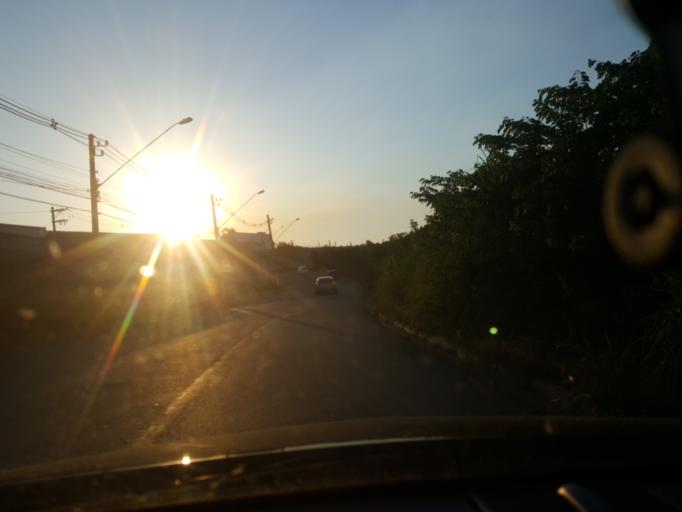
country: BR
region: Sao Paulo
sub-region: Cajamar
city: Cajamar
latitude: -23.3829
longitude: -46.8604
